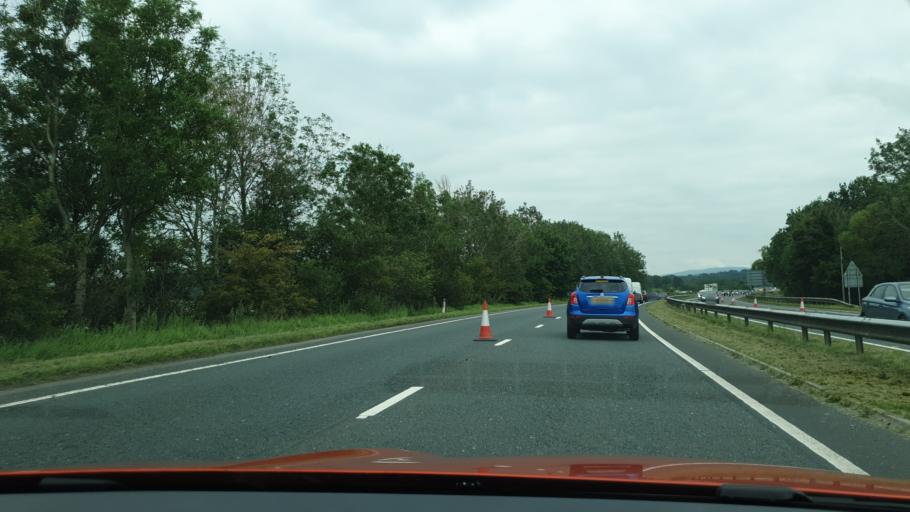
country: GB
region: England
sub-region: Cumbria
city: Milnthorpe
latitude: 54.2619
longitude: -2.8077
